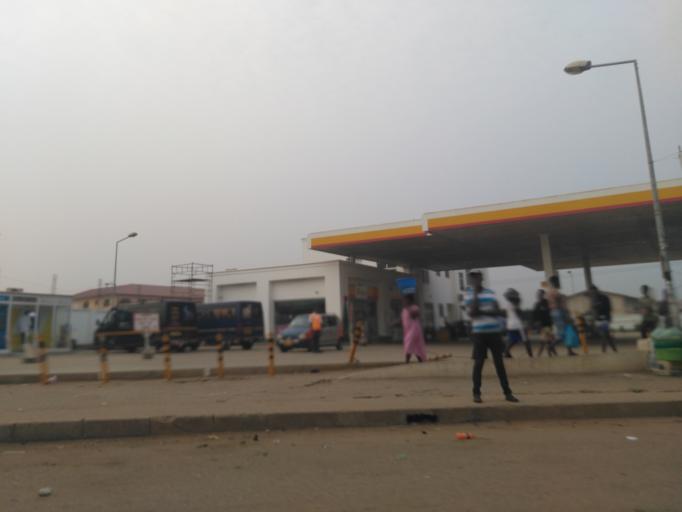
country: GH
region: Greater Accra
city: Dome
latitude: 5.6583
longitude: -0.2666
